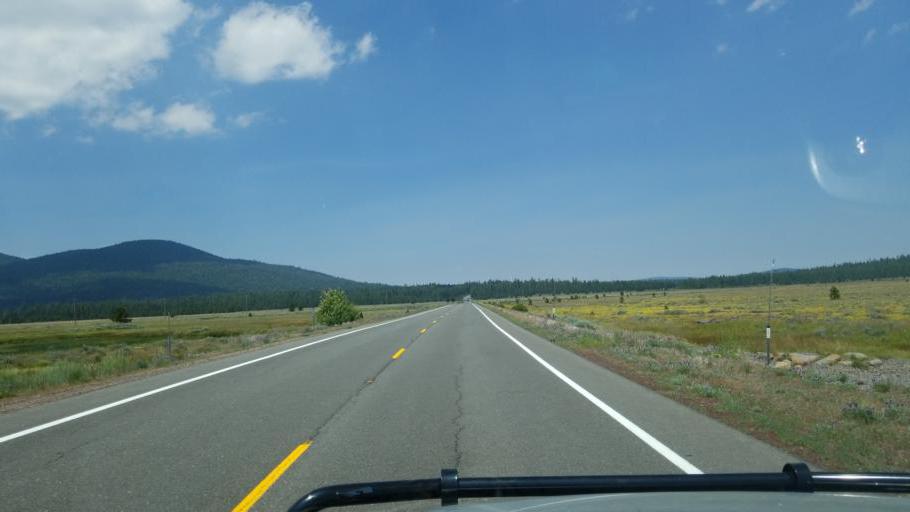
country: US
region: California
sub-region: Lassen County
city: Westwood
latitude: 40.5733
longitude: -121.0750
